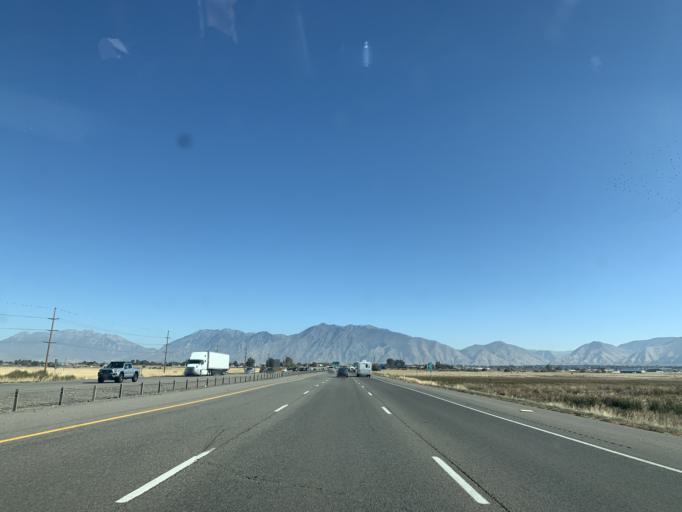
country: US
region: Utah
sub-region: Utah County
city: Payson
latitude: 40.0673
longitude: -111.7210
